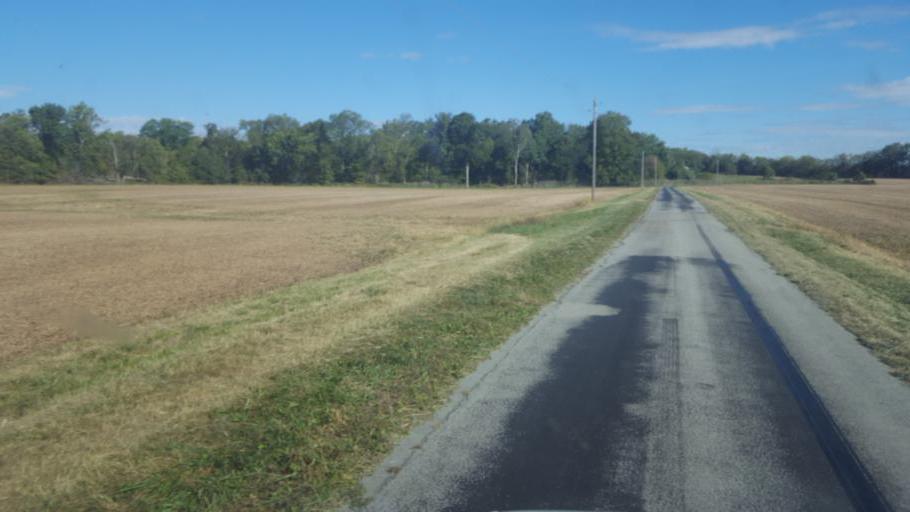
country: US
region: Ohio
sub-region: Wyandot County
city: Upper Sandusky
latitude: 40.7551
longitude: -83.2071
